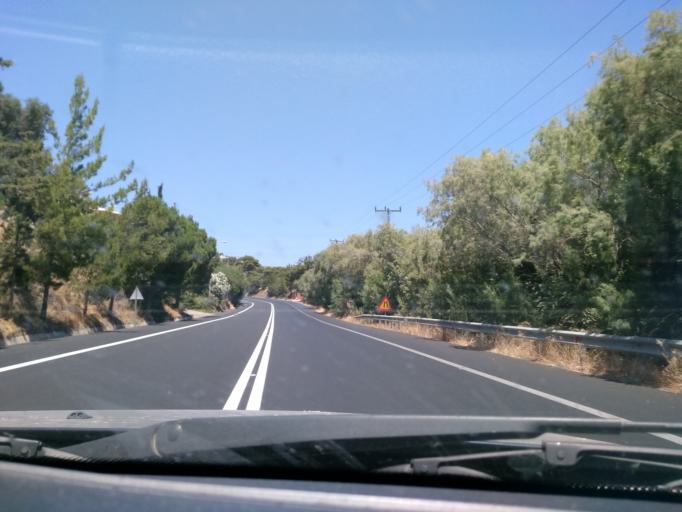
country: GR
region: Crete
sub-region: Nomos Irakleiou
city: Gazi
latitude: 35.3508
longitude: 25.0426
